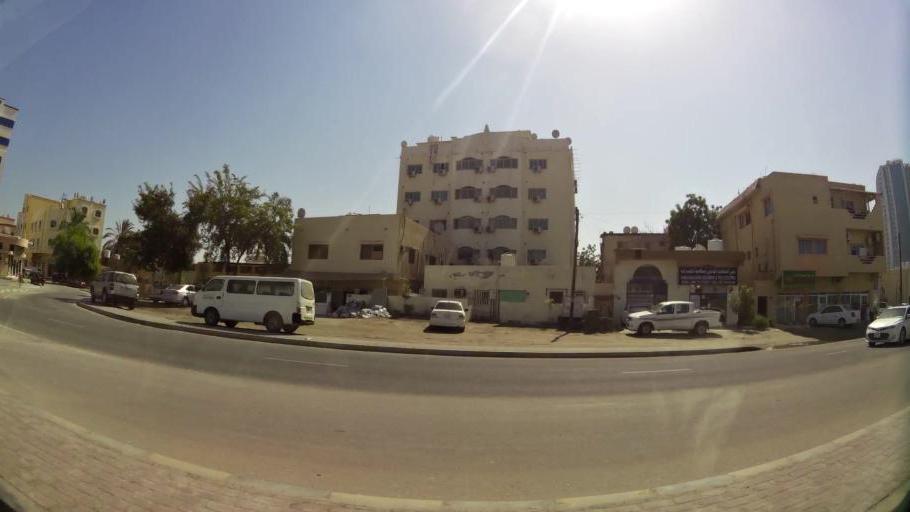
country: AE
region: Ajman
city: Ajman
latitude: 25.4068
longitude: 55.4481
